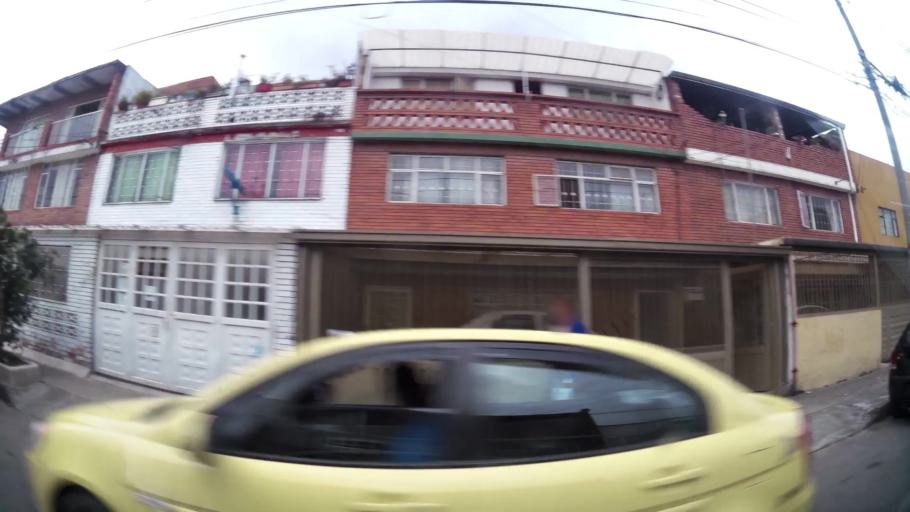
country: CO
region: Bogota D.C.
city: Bogota
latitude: 4.6879
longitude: -74.1038
